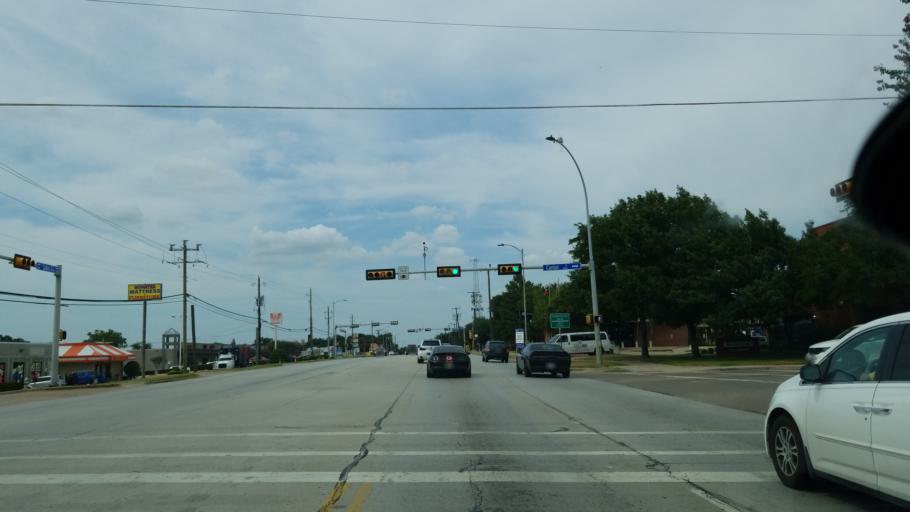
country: US
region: Texas
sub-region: Tarrant County
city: Arlington
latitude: 32.7690
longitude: -97.0971
